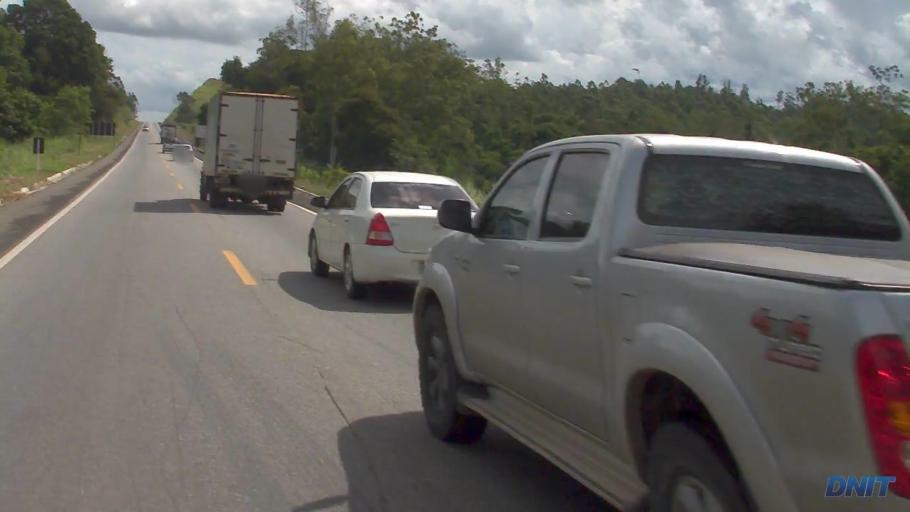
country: BR
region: Minas Gerais
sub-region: Ipatinga
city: Ipatinga
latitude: -19.4309
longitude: -42.5049
